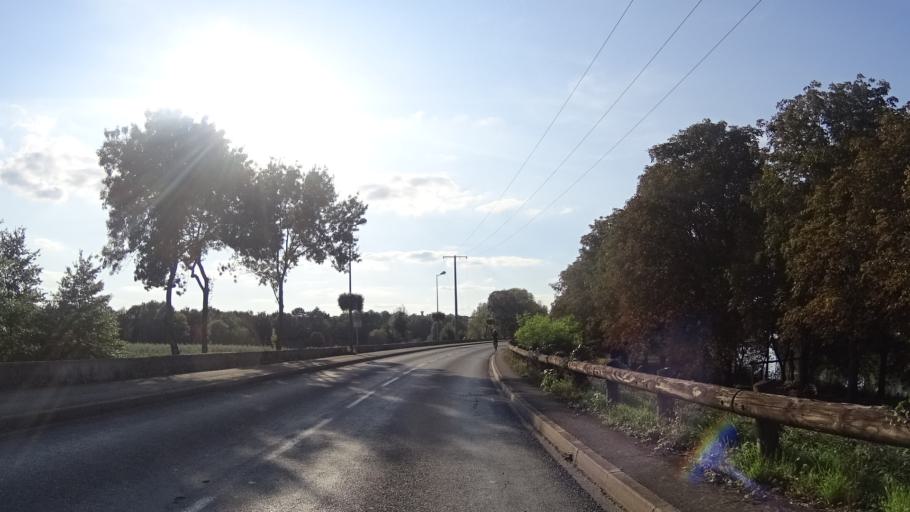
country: FR
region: Pays de la Loire
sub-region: Departement de Maine-et-Loire
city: Chalonnes-sur-Loire
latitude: 47.3500
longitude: -0.7503
